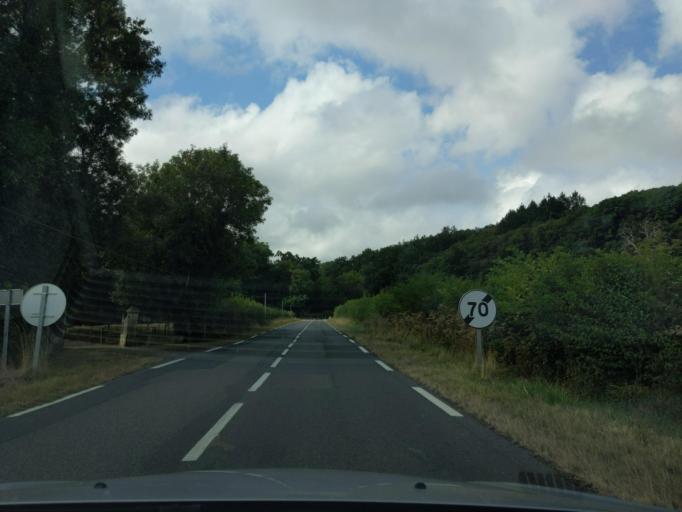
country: FR
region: Bourgogne
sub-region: Departement de la Nievre
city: Luzy
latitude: 46.7826
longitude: 3.9604
